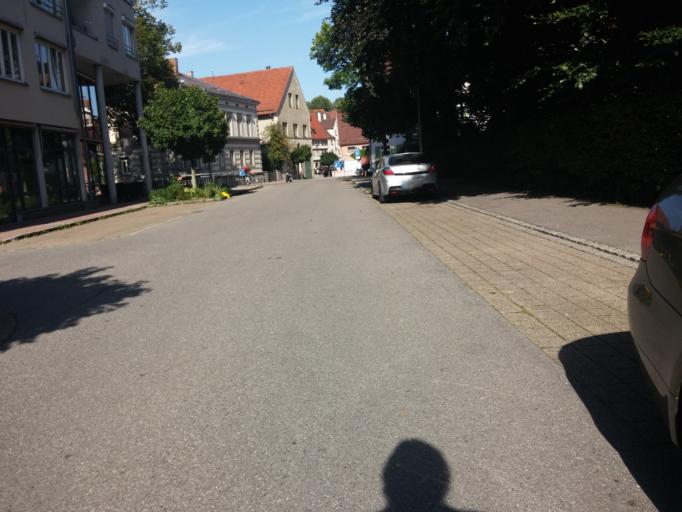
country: DE
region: Baden-Wuerttemberg
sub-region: Tuebingen Region
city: Leutkirch im Allgau
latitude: 47.8260
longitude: 10.0211
